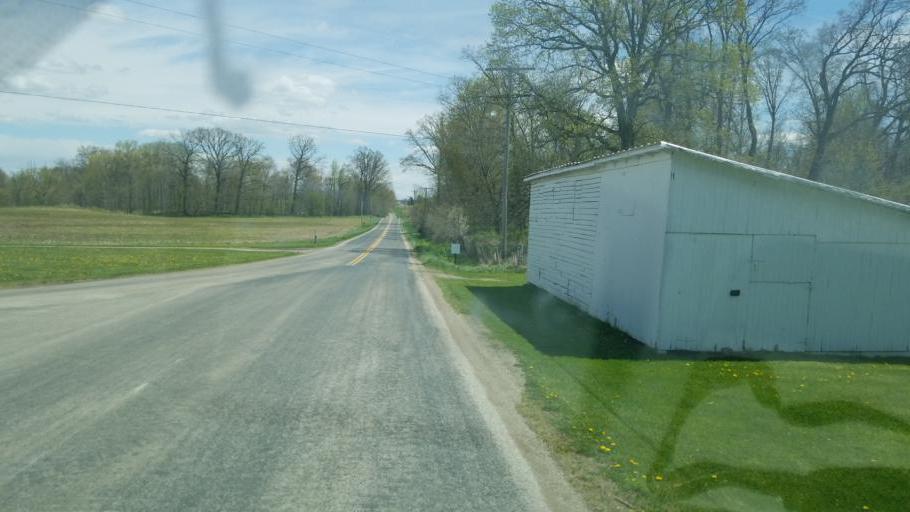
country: US
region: Ohio
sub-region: Ashland County
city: Loudonville
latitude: 40.7620
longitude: -82.1567
